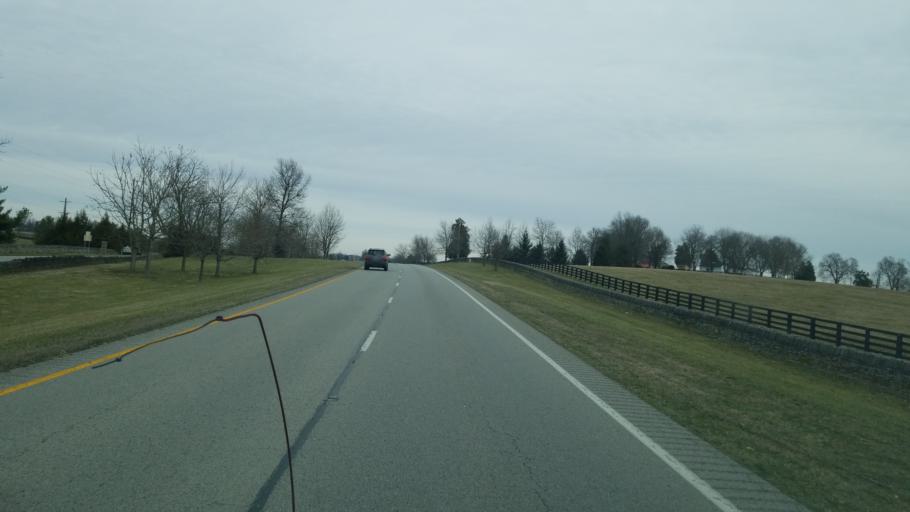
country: US
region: Kentucky
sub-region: Fayette County
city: Lexington-Fayette
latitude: 38.1197
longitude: -84.3886
